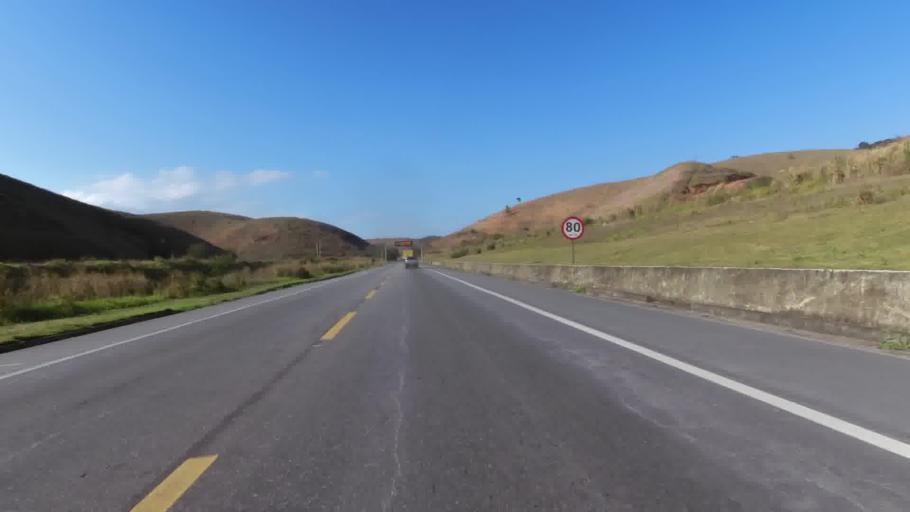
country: BR
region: Espirito Santo
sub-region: Mimoso Do Sul
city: Mimoso do Sul
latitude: -21.1941
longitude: -41.2978
